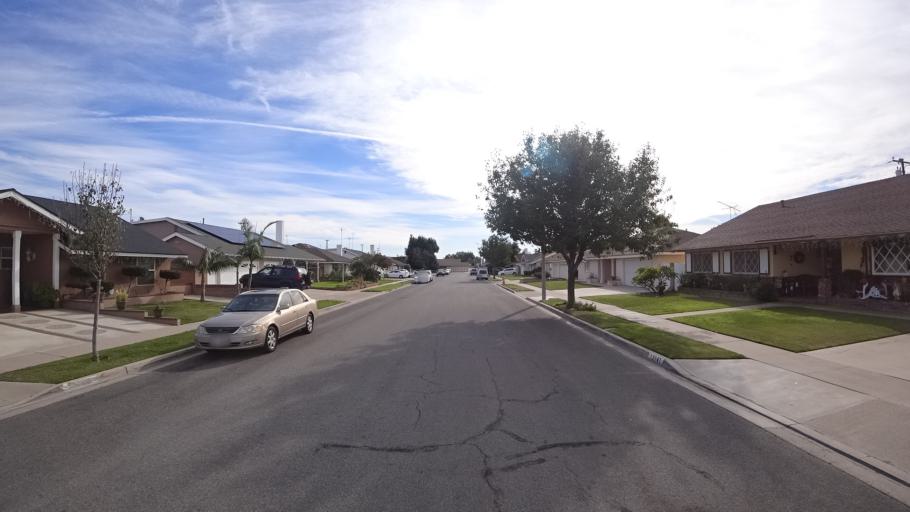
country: US
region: California
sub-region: Orange County
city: Garden Grove
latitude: 33.7724
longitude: -117.9065
